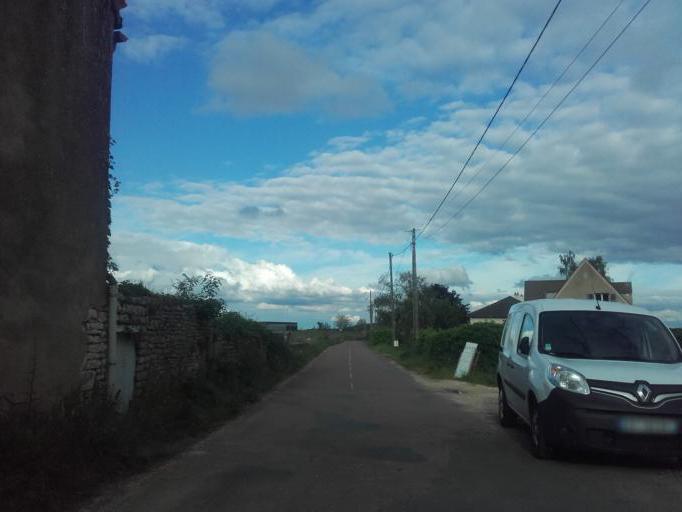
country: FR
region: Bourgogne
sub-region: Departement de Saone-et-Loire
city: Mellecey
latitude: 46.8297
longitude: 4.7391
